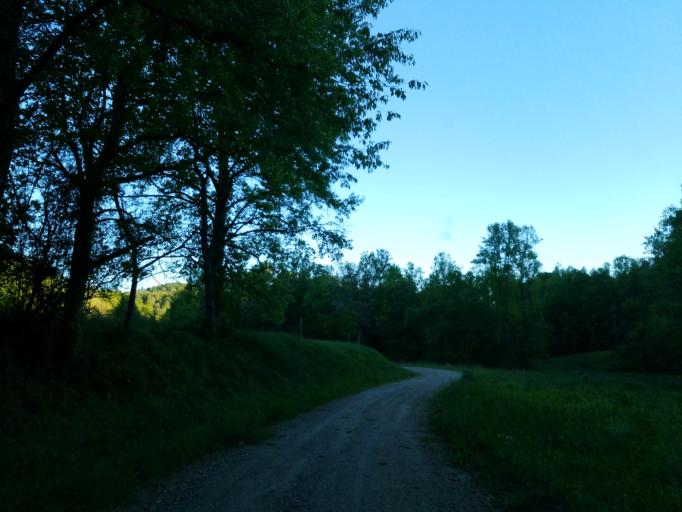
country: US
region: Georgia
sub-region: Union County
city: Blairsville
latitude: 34.7283
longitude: -84.0597
